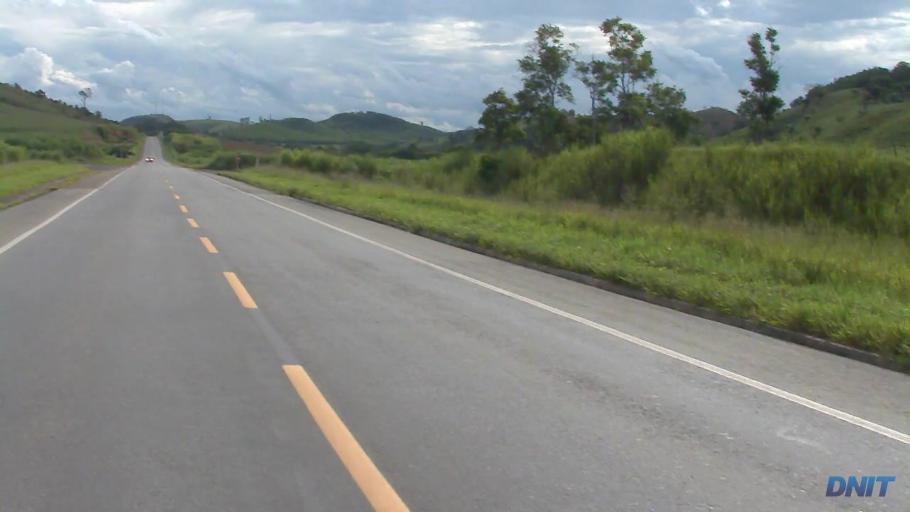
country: BR
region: Minas Gerais
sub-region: Belo Oriente
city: Belo Oriente
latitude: -19.1968
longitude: -42.2830
